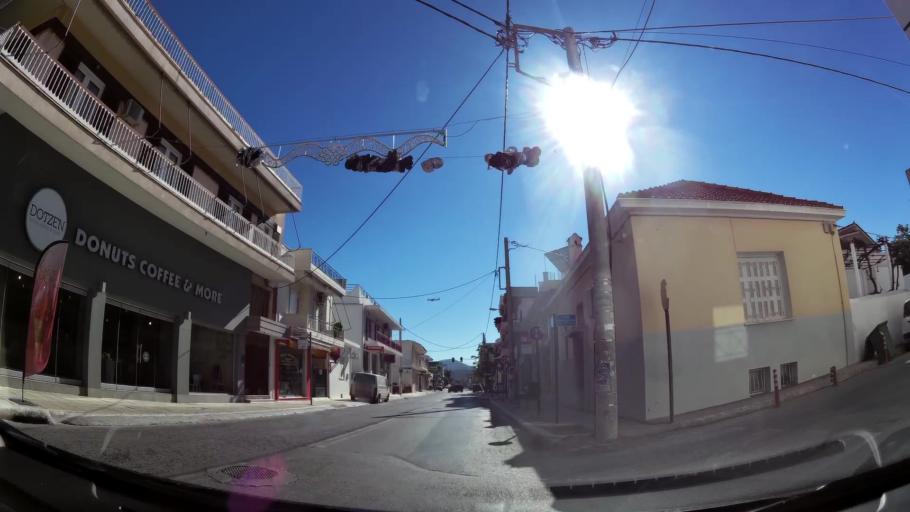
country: GR
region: Attica
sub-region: Nomarchia Anatolikis Attikis
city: Koropi
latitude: 37.8958
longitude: 23.8772
